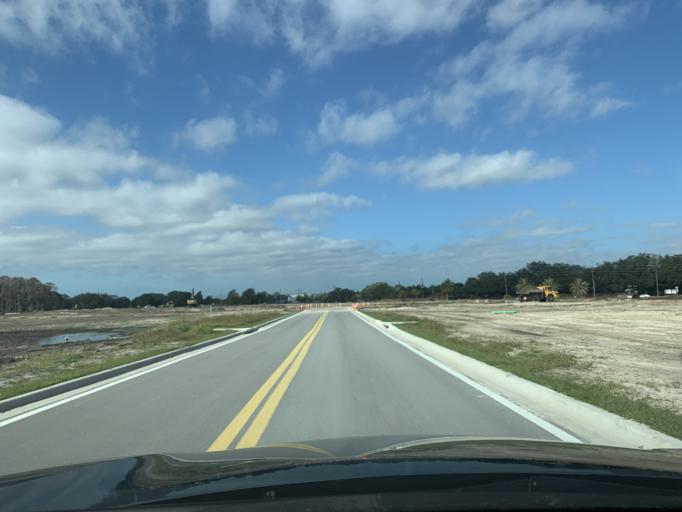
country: US
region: Florida
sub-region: Pasco County
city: Trinity
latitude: 28.2041
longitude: -82.6712
